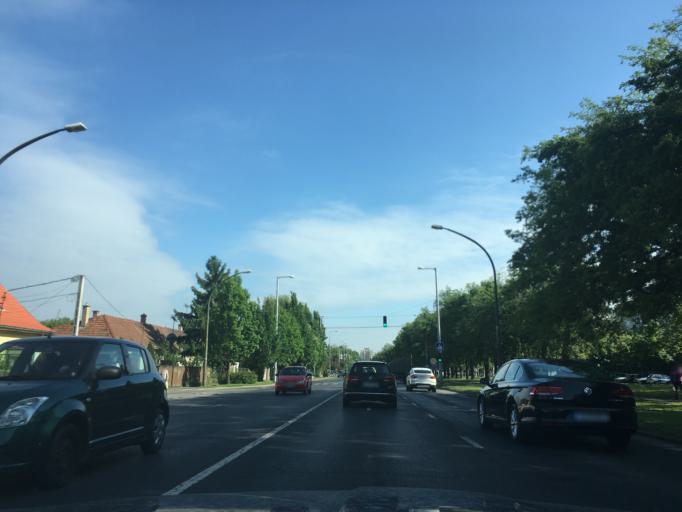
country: HU
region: Hajdu-Bihar
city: Debrecen
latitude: 47.5453
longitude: 21.6097
